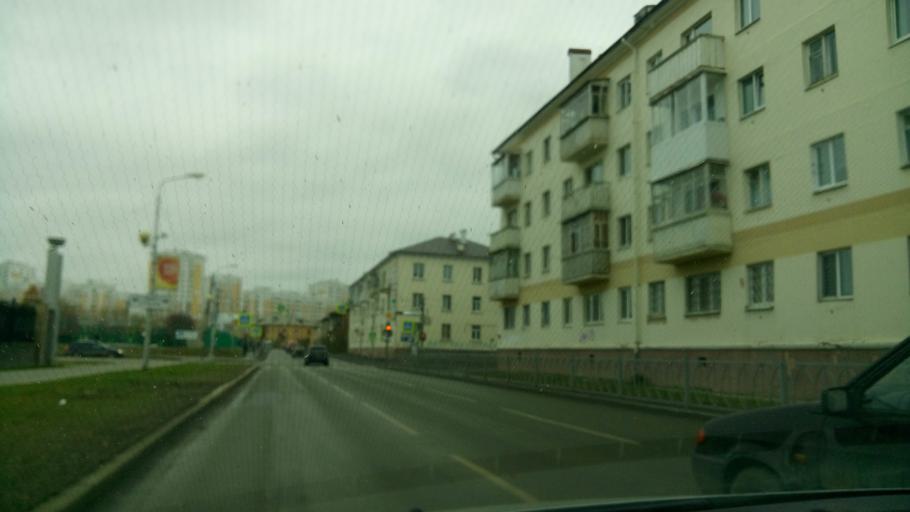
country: RU
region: Sverdlovsk
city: Verkhnyaya Pyshma
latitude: 56.9686
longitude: 60.5799
